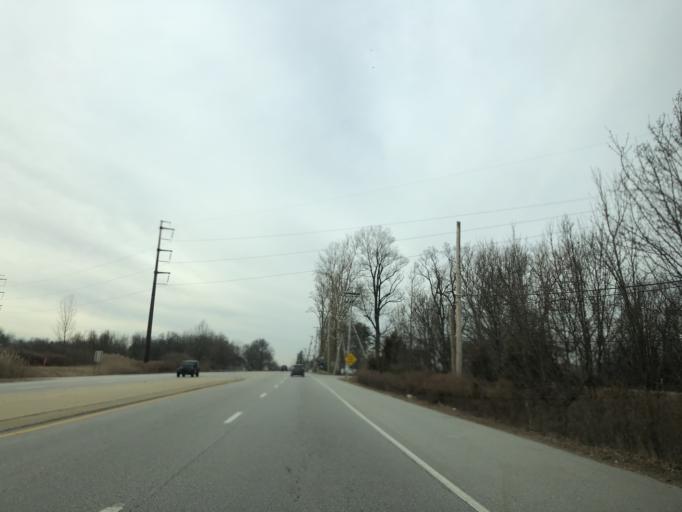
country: US
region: Pennsylvania
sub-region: Chester County
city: Exton
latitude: 40.0328
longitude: -75.5877
